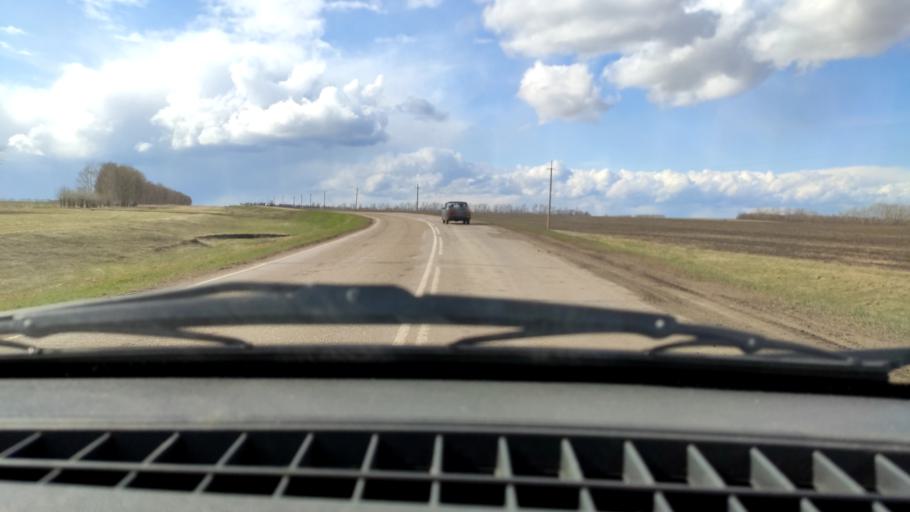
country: RU
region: Bashkortostan
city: Kushnarenkovo
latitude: 55.0980
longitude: 55.0485
